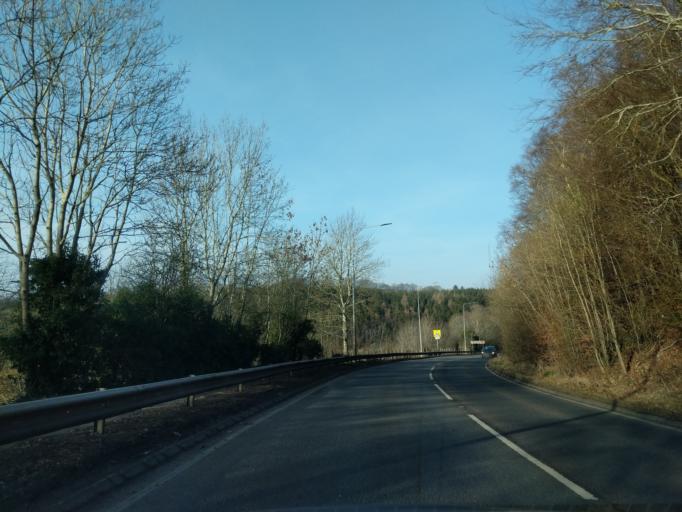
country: GB
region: Scotland
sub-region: South Lanarkshire
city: Lanark
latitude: 55.6780
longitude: -3.7966
